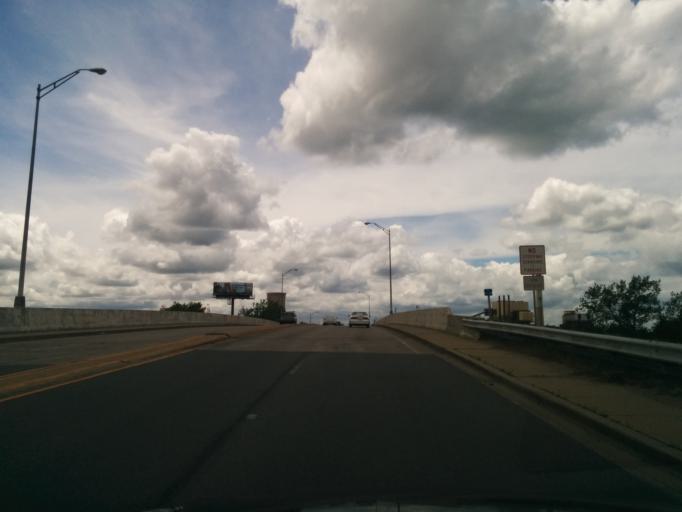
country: US
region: Indiana
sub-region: LaPorte County
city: Michigan City
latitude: 41.7213
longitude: -86.8952
